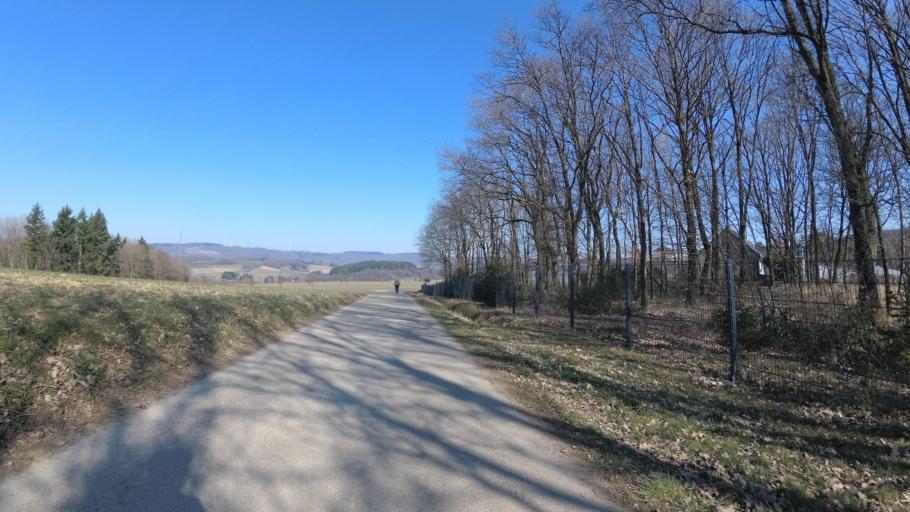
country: DE
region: Rheinland-Pfalz
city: Herchweiler
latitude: 49.5060
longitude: 7.2908
